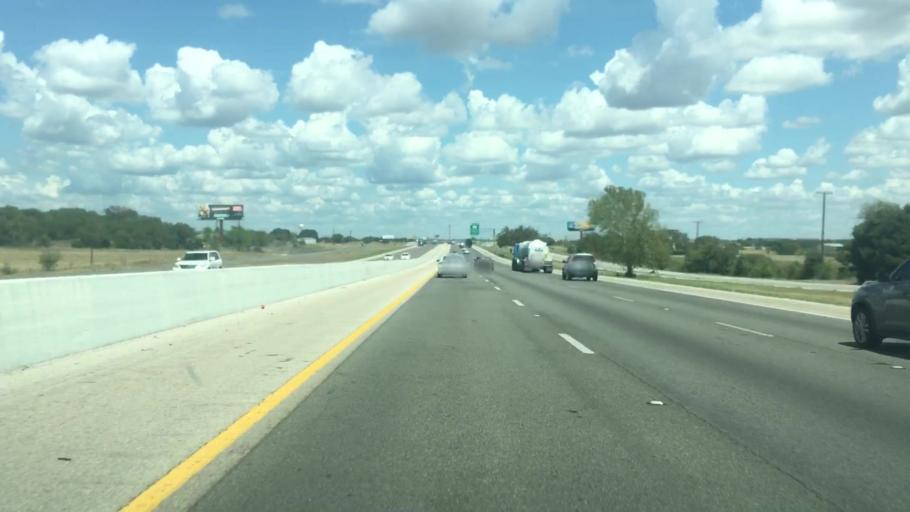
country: US
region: Texas
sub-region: Williamson County
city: Serenada
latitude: 30.7948
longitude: -97.6195
